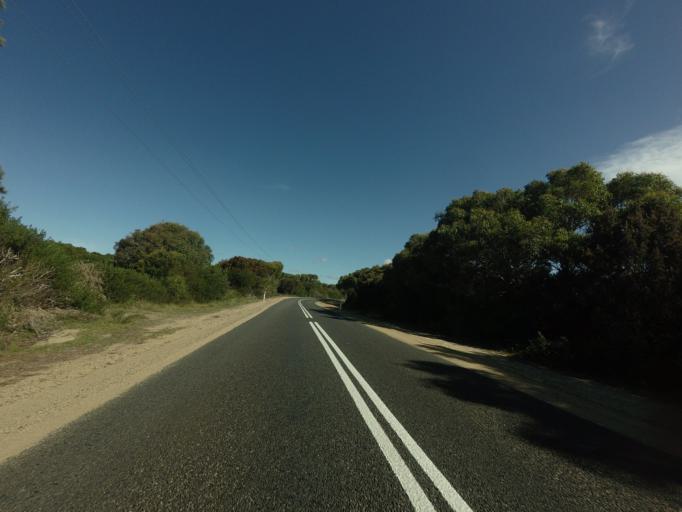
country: AU
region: Tasmania
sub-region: Break O'Day
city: St Helens
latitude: -41.8255
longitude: 148.2629
